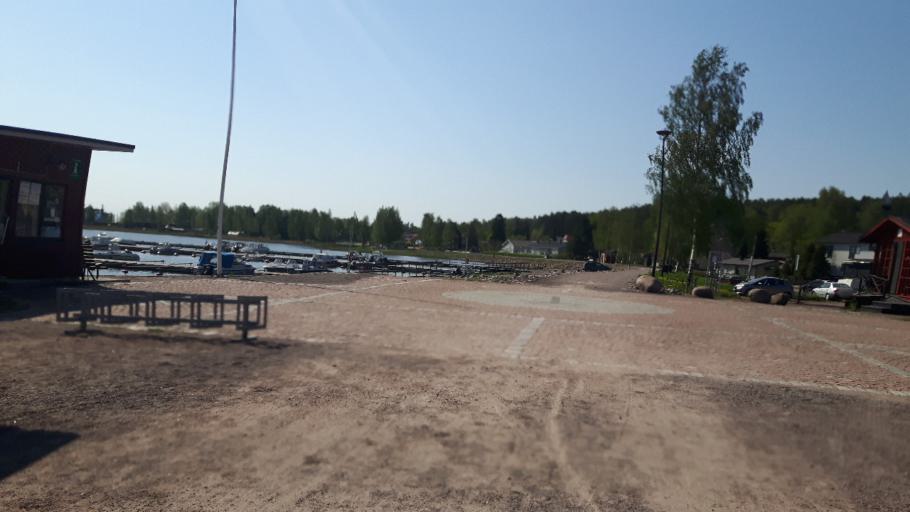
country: FI
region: Uusimaa
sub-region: Loviisa
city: Lovisa
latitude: 60.4523
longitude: 26.2347
